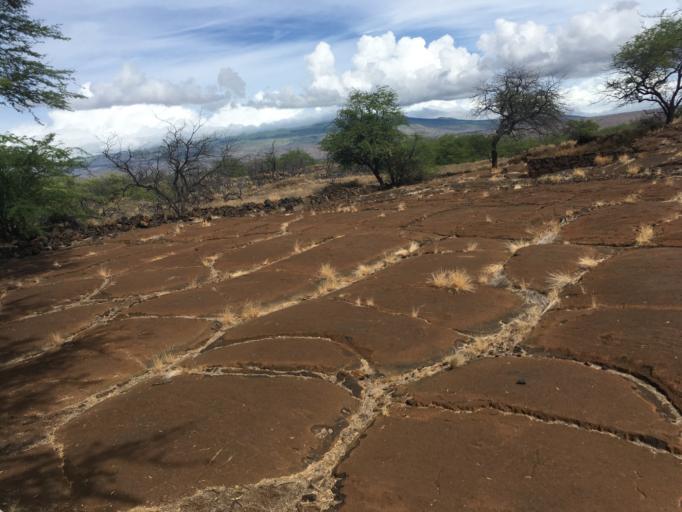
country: US
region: Hawaii
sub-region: Hawaii County
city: Waikoloa Village
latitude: 19.9543
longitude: -155.8532
